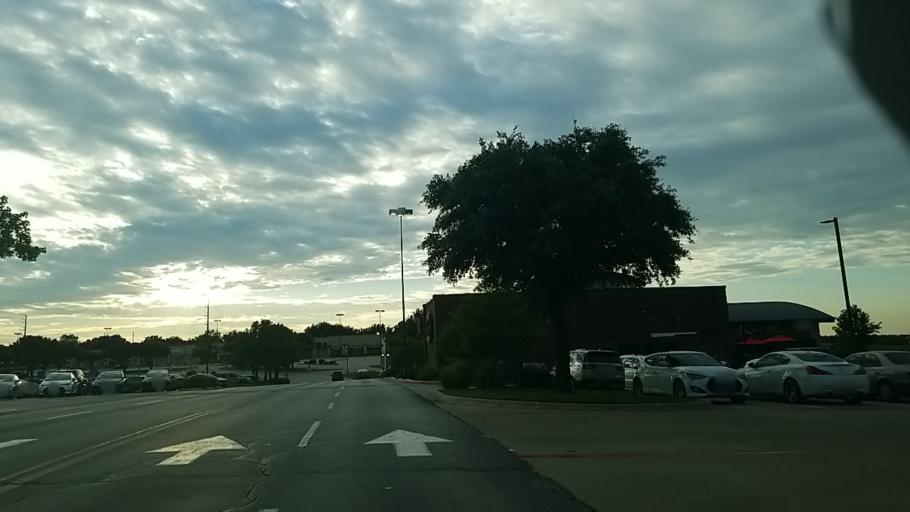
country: US
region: Texas
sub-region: Denton County
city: Lewisville
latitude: 33.0045
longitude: -96.9703
